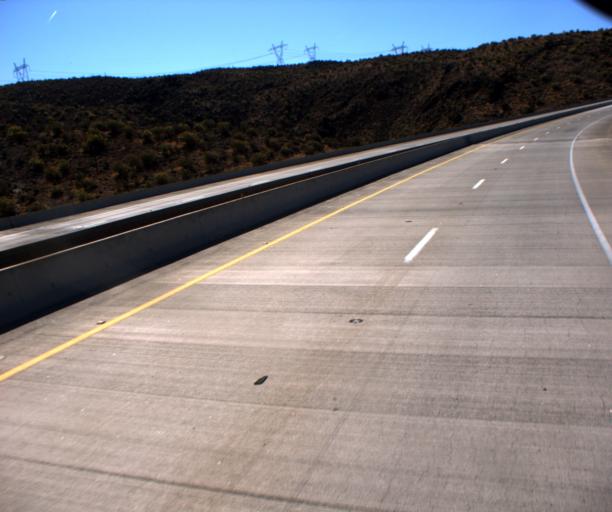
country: US
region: Arizona
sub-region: Yavapai County
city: Bagdad
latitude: 34.5790
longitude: -113.4918
